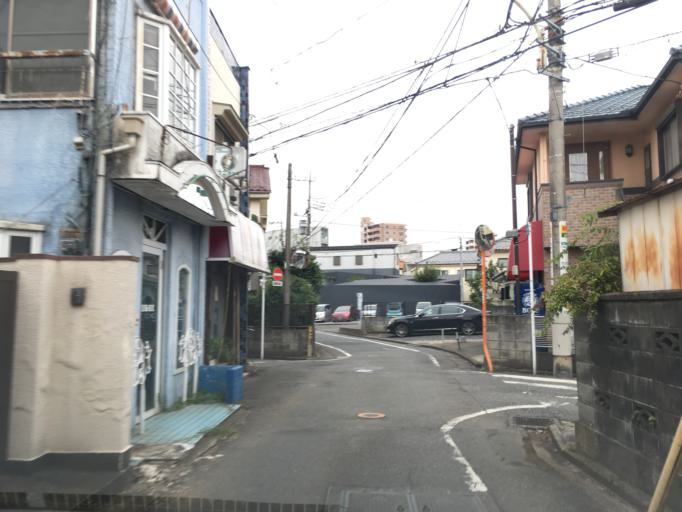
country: JP
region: Tokyo
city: Higashimurayama-shi
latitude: 35.7603
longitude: 139.4638
